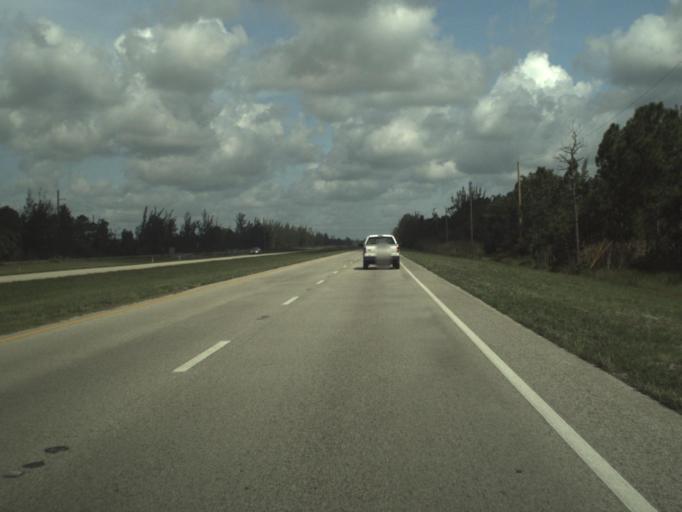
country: US
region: Florida
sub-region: Palm Beach County
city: Limestone Creek
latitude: 26.8813
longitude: -80.2589
